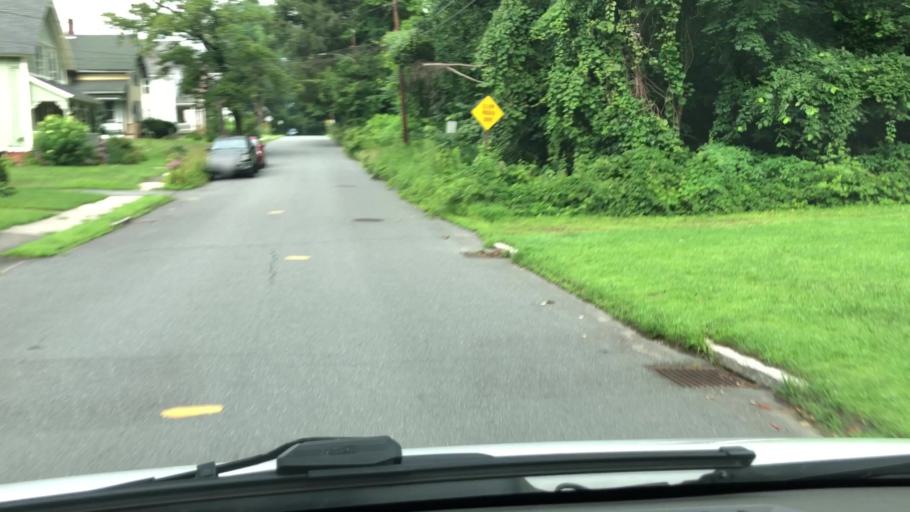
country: US
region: Massachusetts
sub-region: Franklin County
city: Greenfield
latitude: 42.5951
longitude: -72.6021
